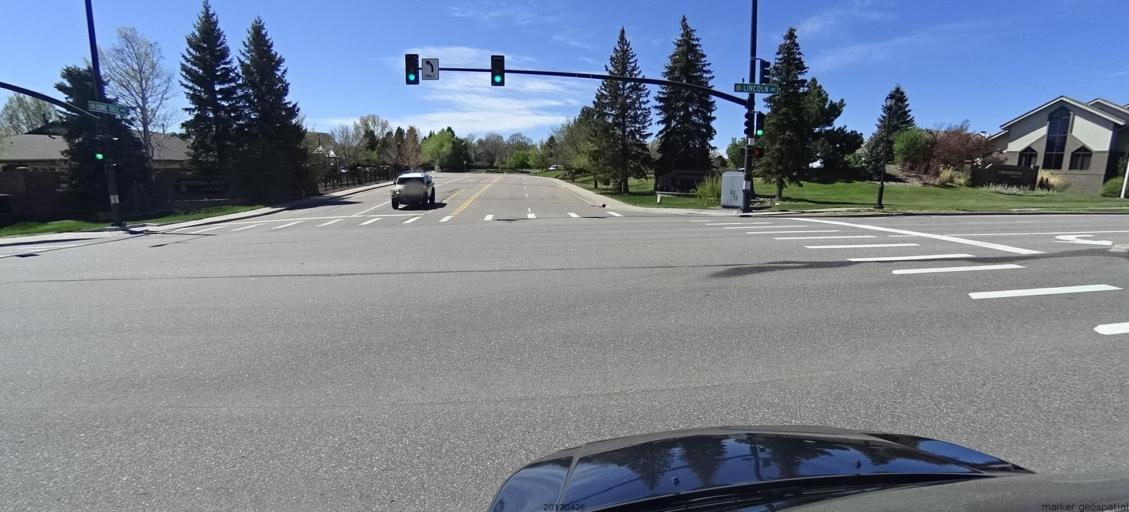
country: US
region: Colorado
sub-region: Douglas County
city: Carriage Club
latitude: 39.5366
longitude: -104.9023
